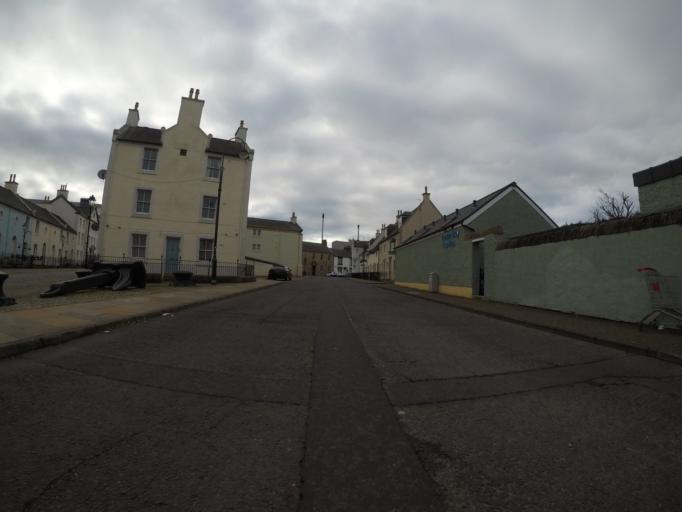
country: GB
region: Scotland
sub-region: North Ayrshire
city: Irvine
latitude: 55.6101
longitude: -4.6783
